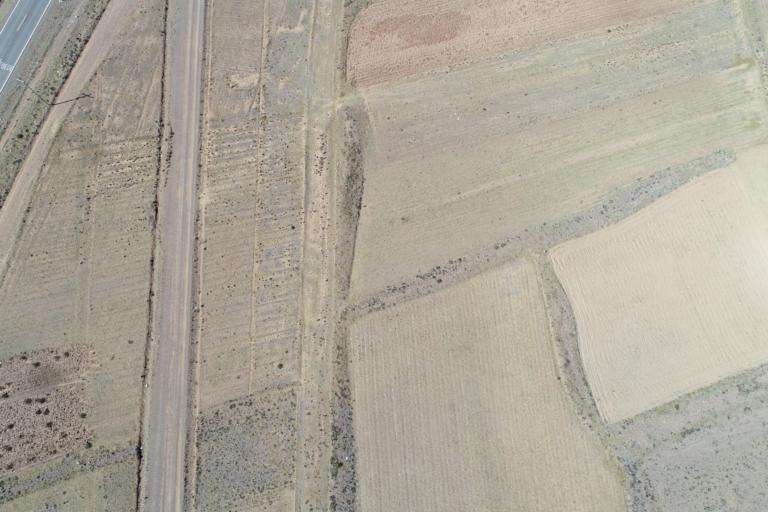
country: BO
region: La Paz
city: Achacachi
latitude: -15.9026
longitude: -68.8998
